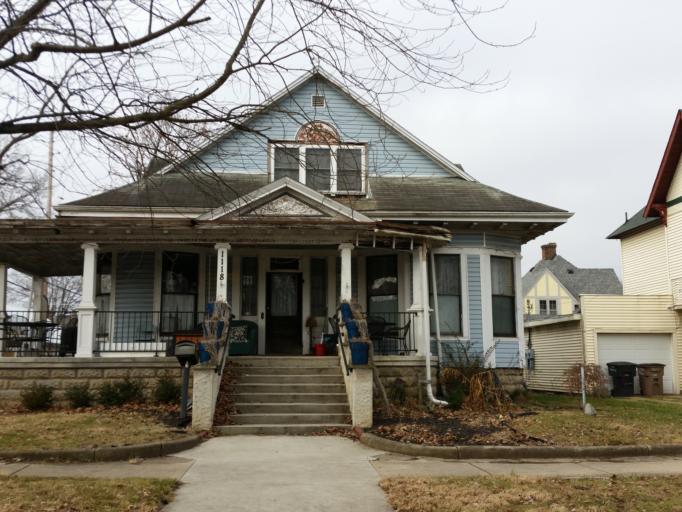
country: US
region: Indiana
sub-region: Bartholomew County
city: Columbus
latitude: 39.2102
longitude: -85.9188
